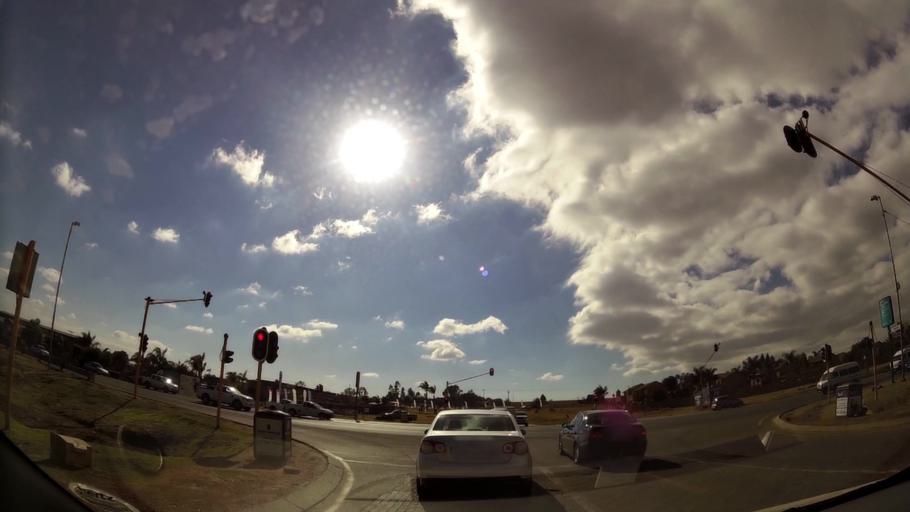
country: ZA
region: Gauteng
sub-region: West Rand District Municipality
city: Muldersdriseloop
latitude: -26.0694
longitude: 27.8500
